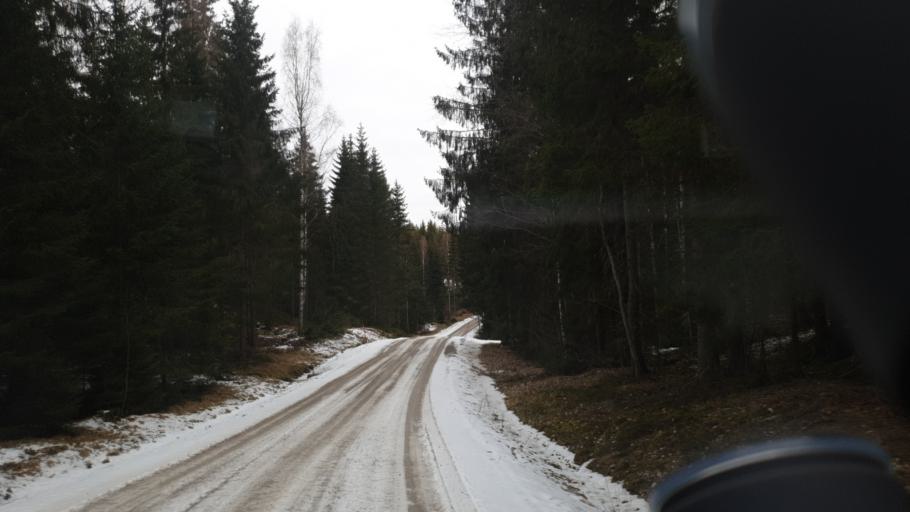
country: SE
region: Vaermland
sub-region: Eda Kommun
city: Amotfors
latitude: 59.7969
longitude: 12.4452
